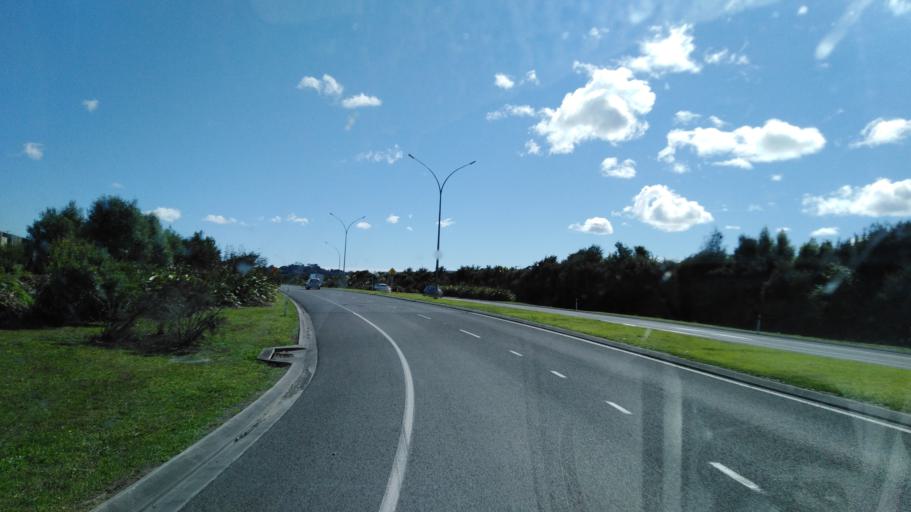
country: NZ
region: Bay of Plenty
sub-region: Tauranga City
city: Tauranga
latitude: -37.7534
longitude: 176.1029
